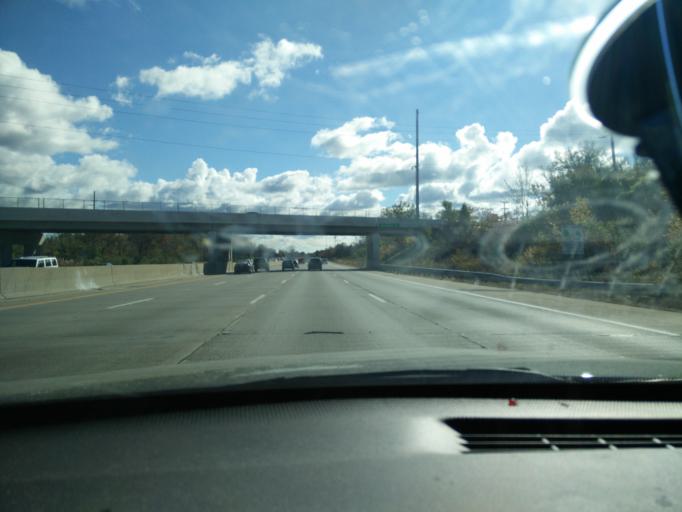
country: US
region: Michigan
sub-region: Oakland County
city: Farmington Hills
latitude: 42.4930
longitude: -83.3397
